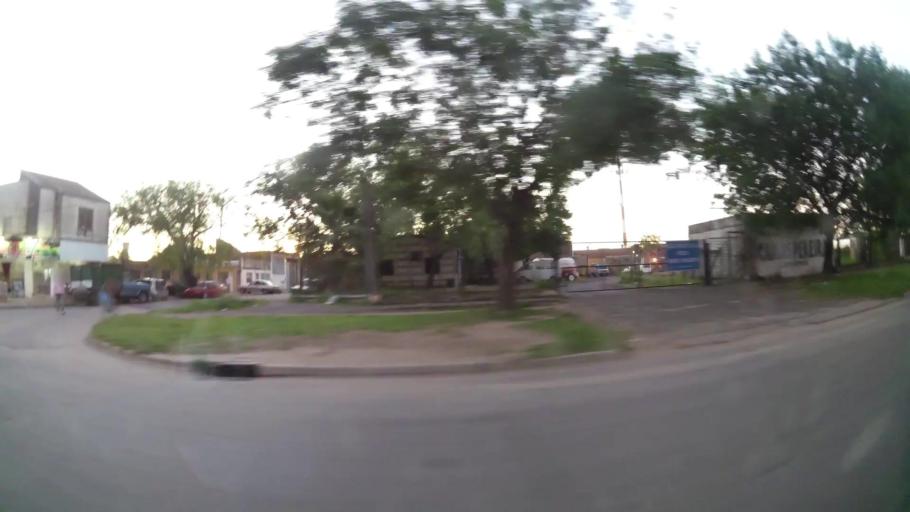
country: AR
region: Santa Fe
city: Santa Fe de la Vera Cruz
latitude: -31.6033
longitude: -60.7127
